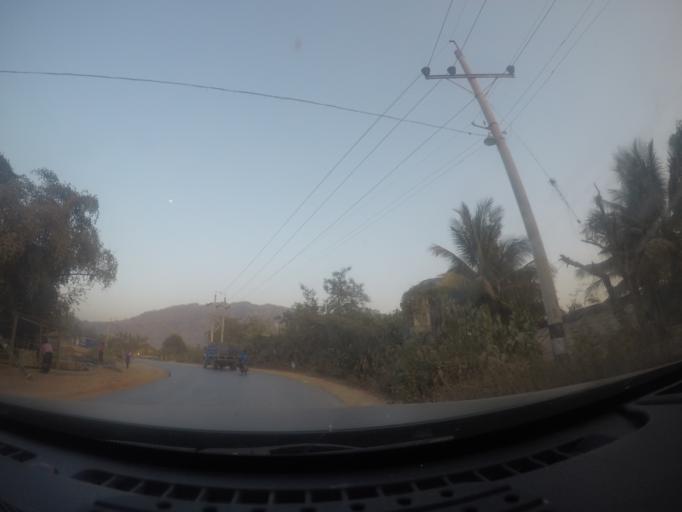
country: MM
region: Mandalay
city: Yamethin
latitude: 20.8172
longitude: 96.3899
